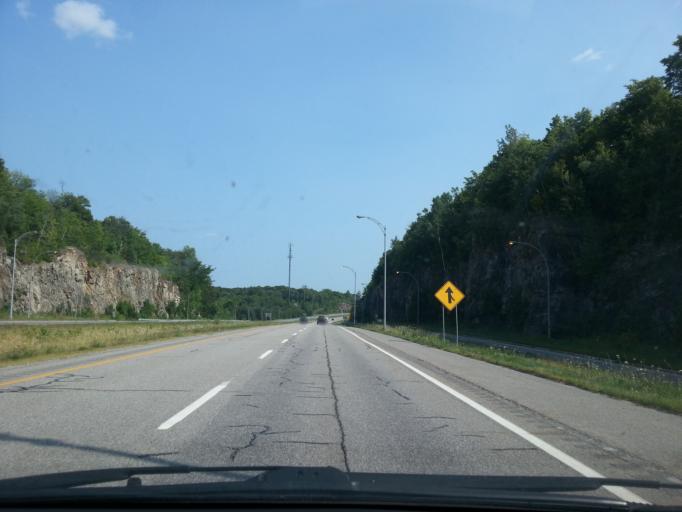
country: CA
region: Quebec
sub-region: Outaouais
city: Gatineau
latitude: 45.5137
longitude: -75.8077
